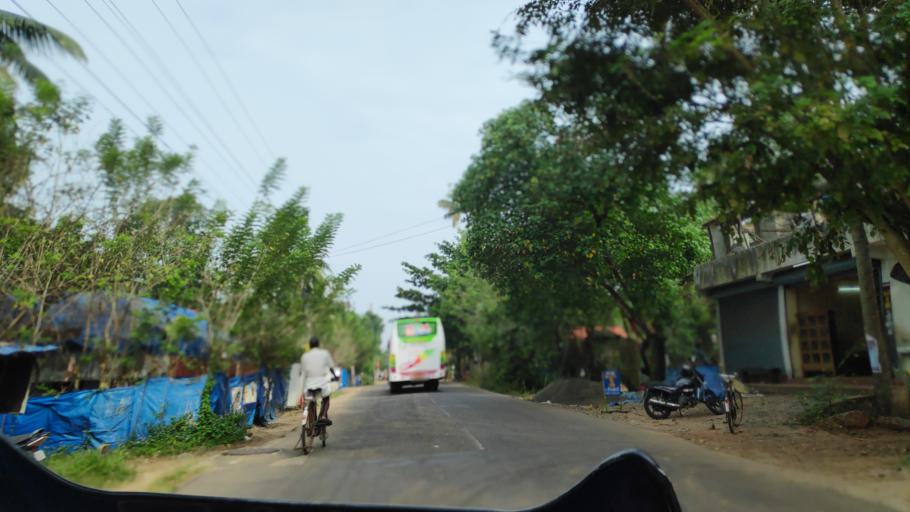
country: IN
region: Kerala
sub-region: Alappuzha
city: Kutiatodu
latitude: 9.8138
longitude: 76.3518
